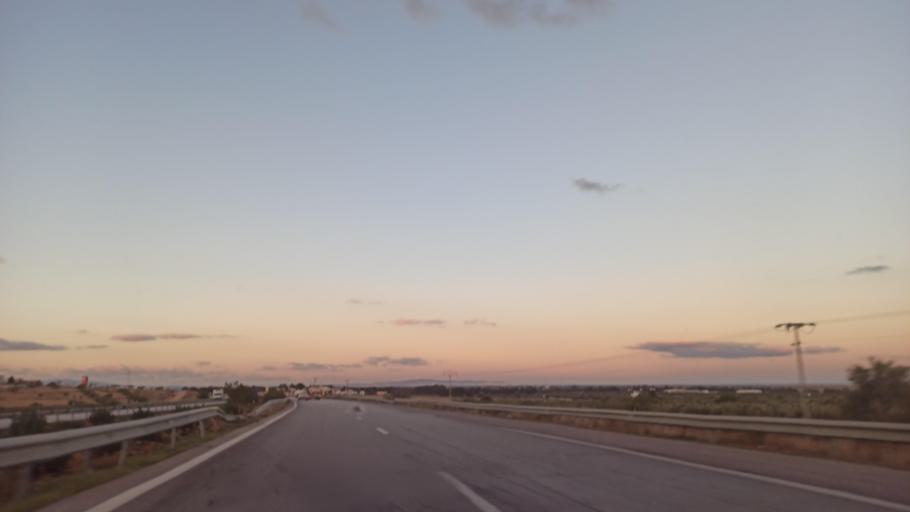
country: TN
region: Susah
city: Harqalah
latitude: 36.2422
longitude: 10.4222
